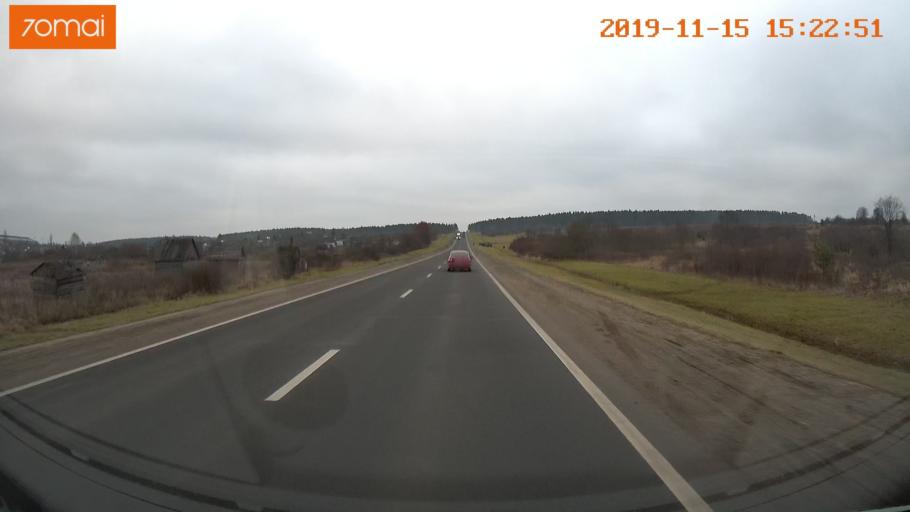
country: RU
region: Jaroslavl
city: Danilov
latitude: 58.1978
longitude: 40.1314
